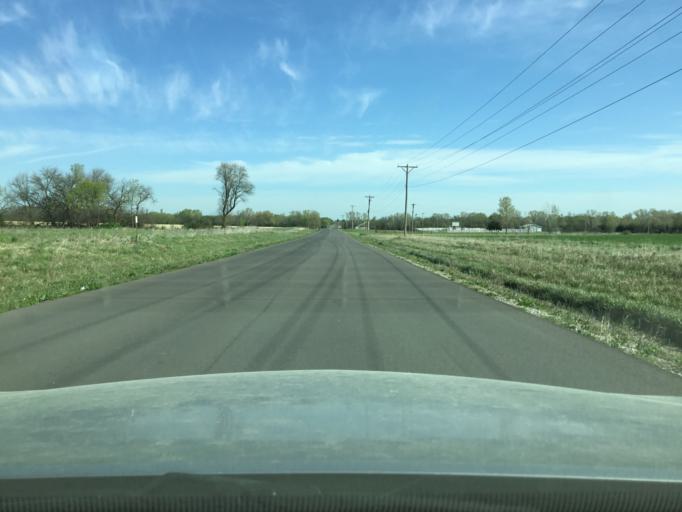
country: US
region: Kansas
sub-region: Neosho County
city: Chanute
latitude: 37.6517
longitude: -95.4435
